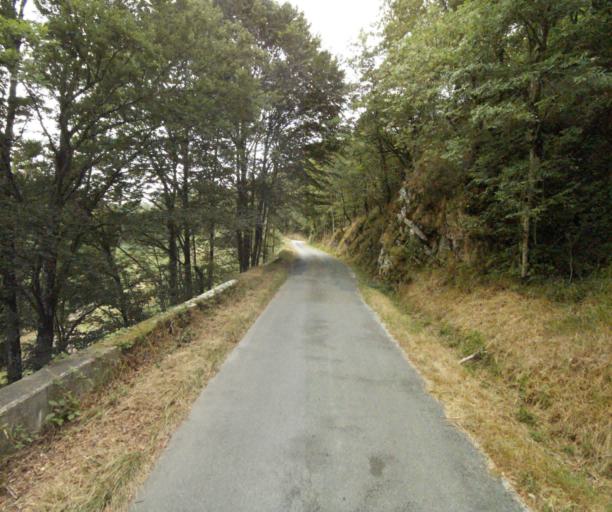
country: FR
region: Midi-Pyrenees
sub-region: Departement du Tarn
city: Soreze
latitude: 43.4179
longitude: 2.0871
